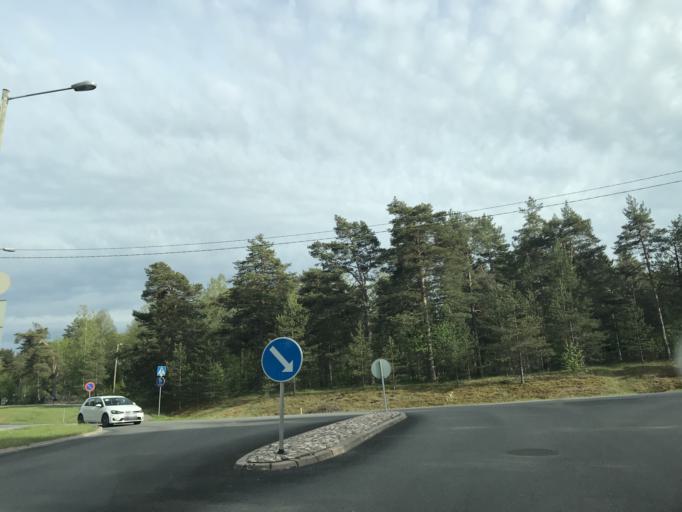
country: FI
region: Varsinais-Suomi
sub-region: Turku
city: Turku
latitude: 60.4369
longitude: 22.3087
